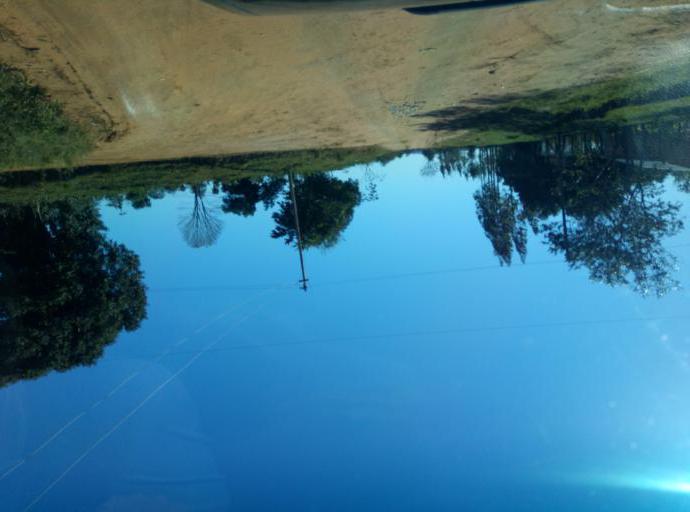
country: PY
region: Caaguazu
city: Doctor Cecilio Baez
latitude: -25.1647
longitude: -56.2322
